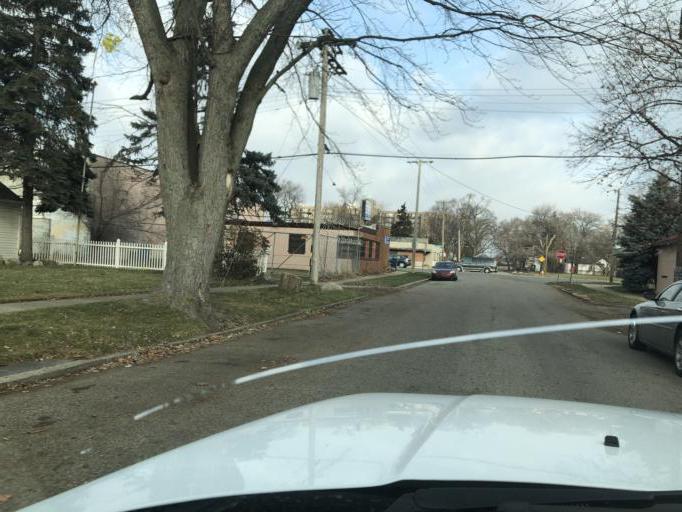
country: US
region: Michigan
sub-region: Oakland County
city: Oak Park
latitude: 42.4150
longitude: -83.2167
